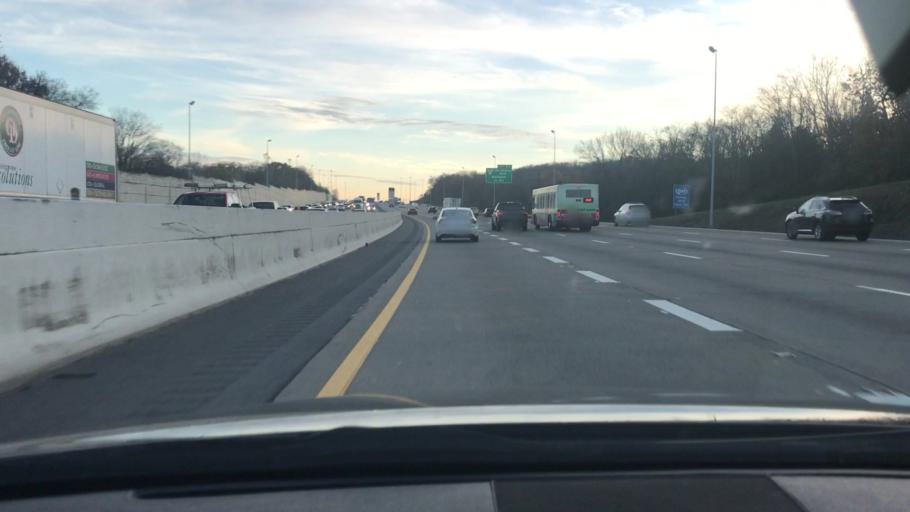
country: US
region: Tennessee
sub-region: Davidson County
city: Goodlettsville
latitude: 36.2766
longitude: -86.7352
